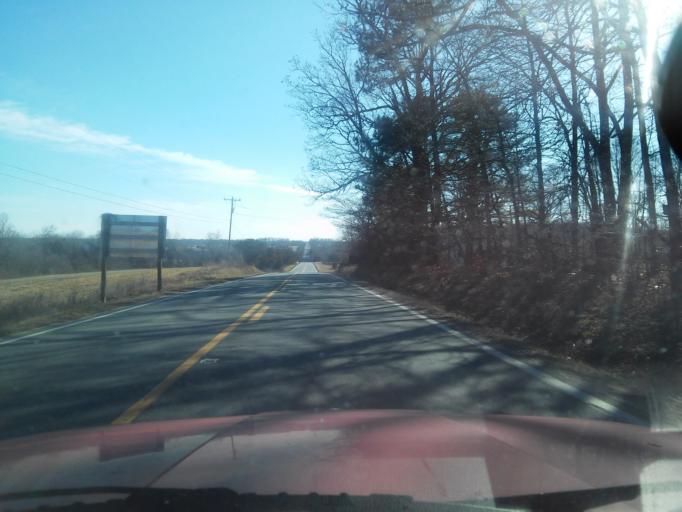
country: US
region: Virginia
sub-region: Orange County
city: Gordonsville
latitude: 38.0669
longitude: -78.1875
